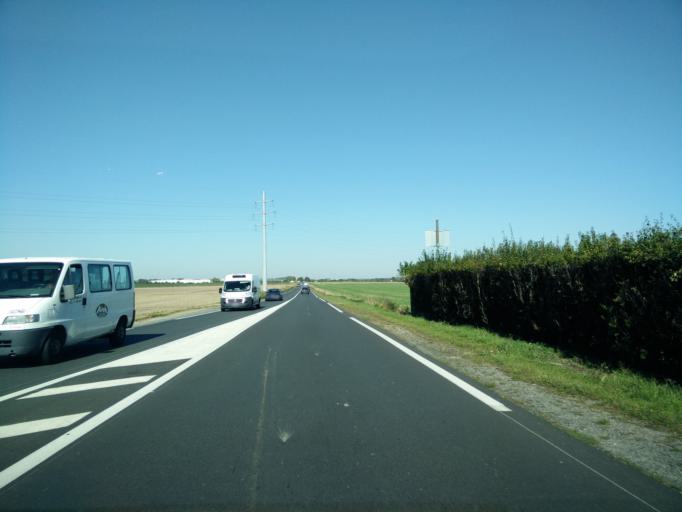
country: FR
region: Ile-de-France
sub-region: Departement de Seine-et-Marne
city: Claye-Souilly
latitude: 48.9702
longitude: 2.6620
